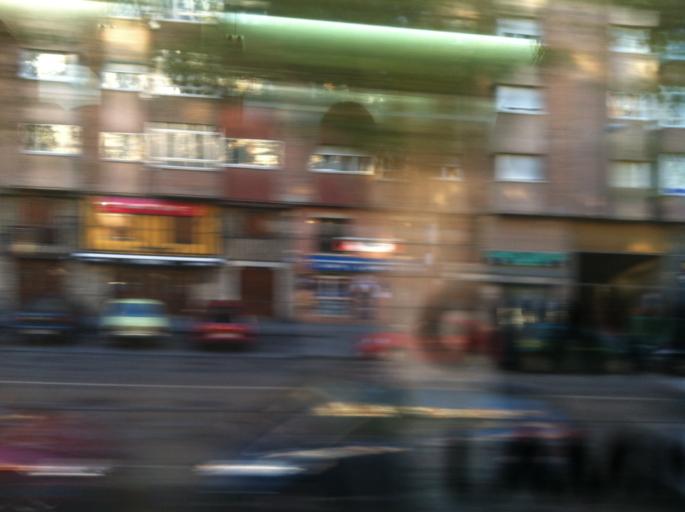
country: ES
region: Castille and Leon
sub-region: Provincia de Valladolid
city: Valladolid
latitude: 41.6460
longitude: -4.7152
